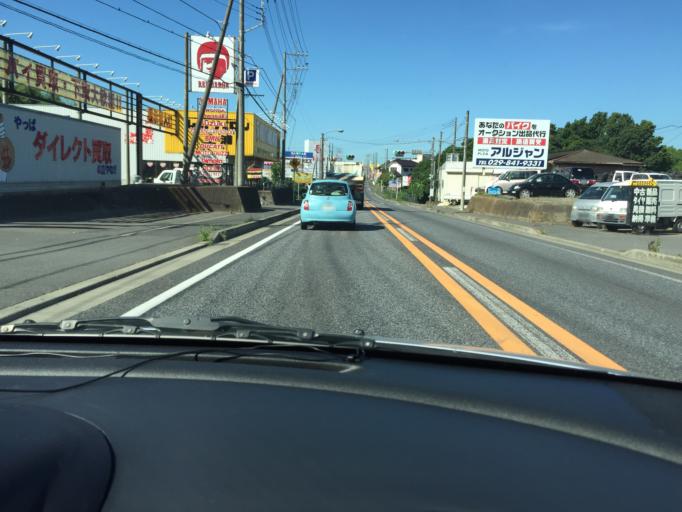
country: JP
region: Ibaraki
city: Naka
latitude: 36.0525
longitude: 140.1731
